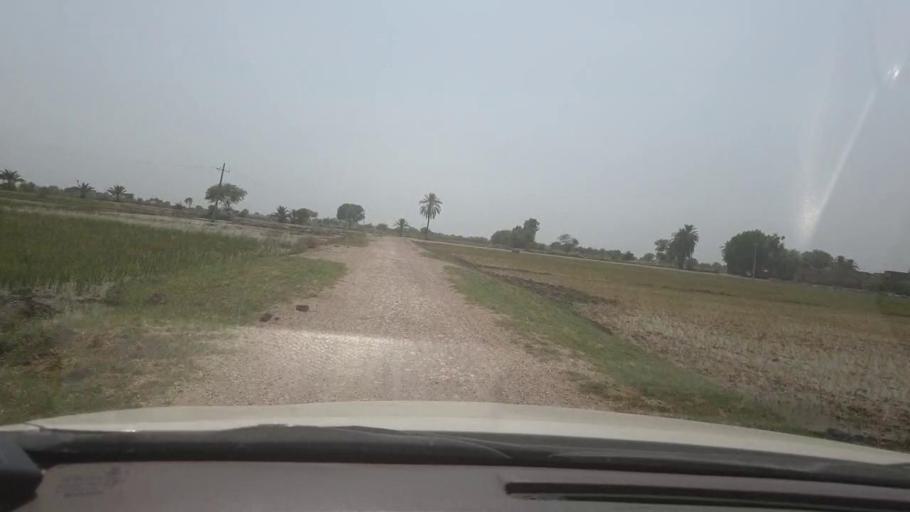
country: PK
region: Sindh
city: Shikarpur
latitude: 27.9625
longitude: 68.5887
